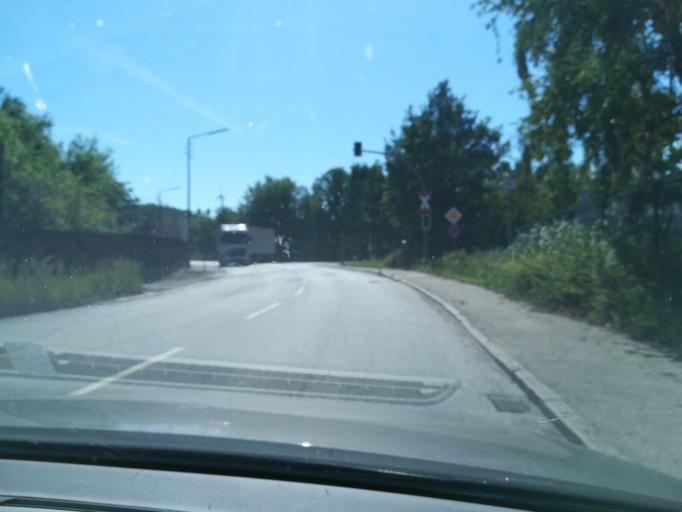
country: DE
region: Hamburg
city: Rothenburgsort
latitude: 53.5119
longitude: 10.0534
